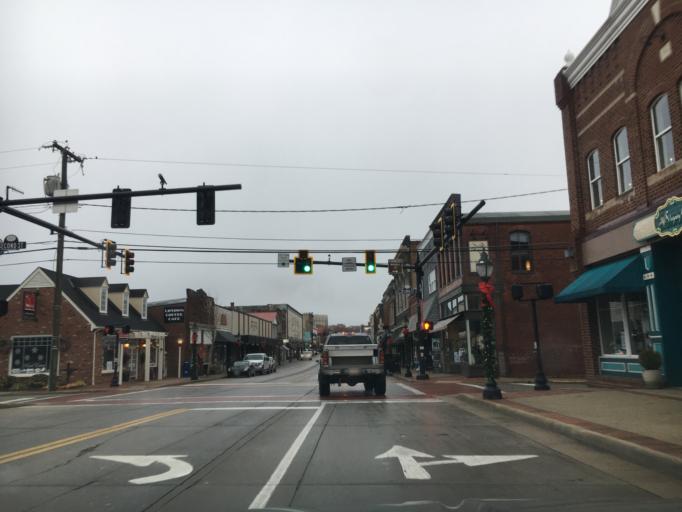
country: US
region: Virginia
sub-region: Prince Edward County
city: Farmville
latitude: 37.3040
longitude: -78.3913
